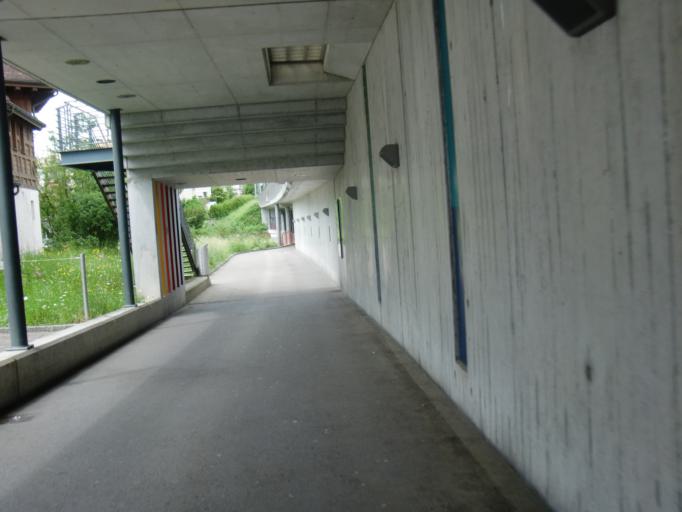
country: CH
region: Zurich
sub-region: Bezirk Hinwil
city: Tann / Tann (Dorfkern)
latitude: 47.2610
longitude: 8.8524
